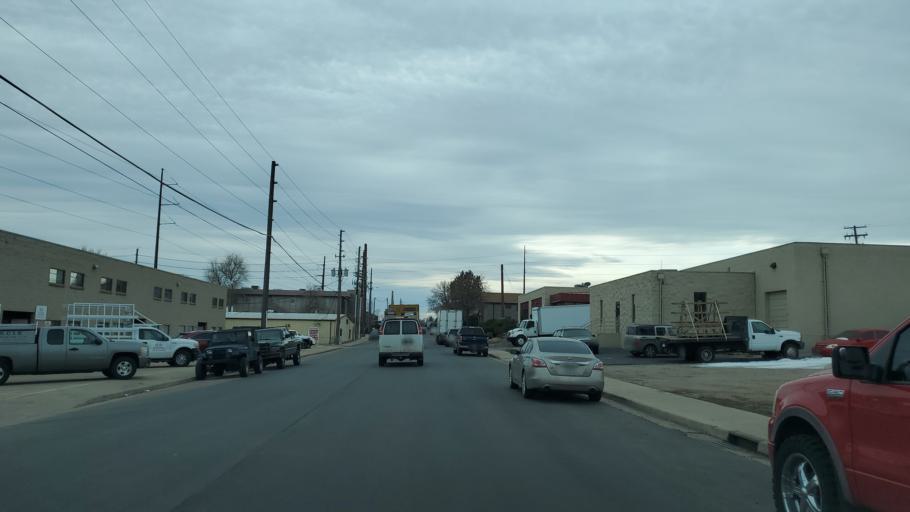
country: US
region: Colorado
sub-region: Denver County
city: Denver
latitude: 39.6960
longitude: -105.0016
